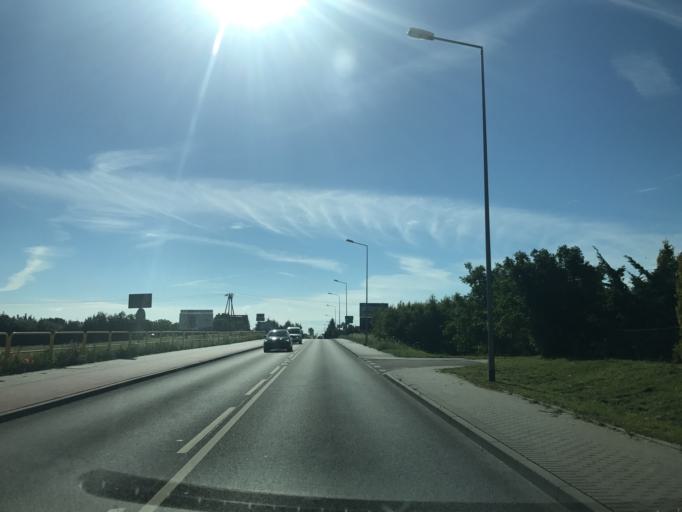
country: PL
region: Pomeranian Voivodeship
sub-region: Powiat chojnicki
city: Chojnice
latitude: 53.6927
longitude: 17.6051
